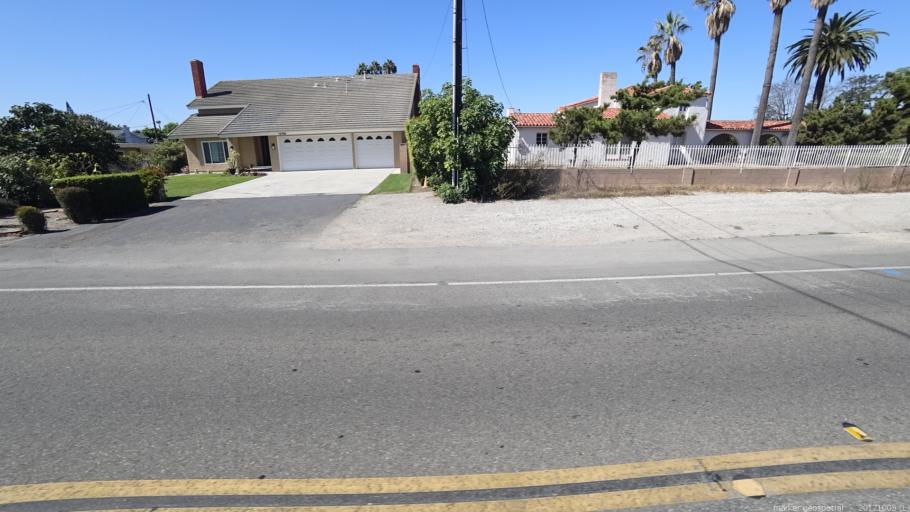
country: US
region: California
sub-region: Orange County
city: Garden Grove
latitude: 33.7769
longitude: -117.9672
